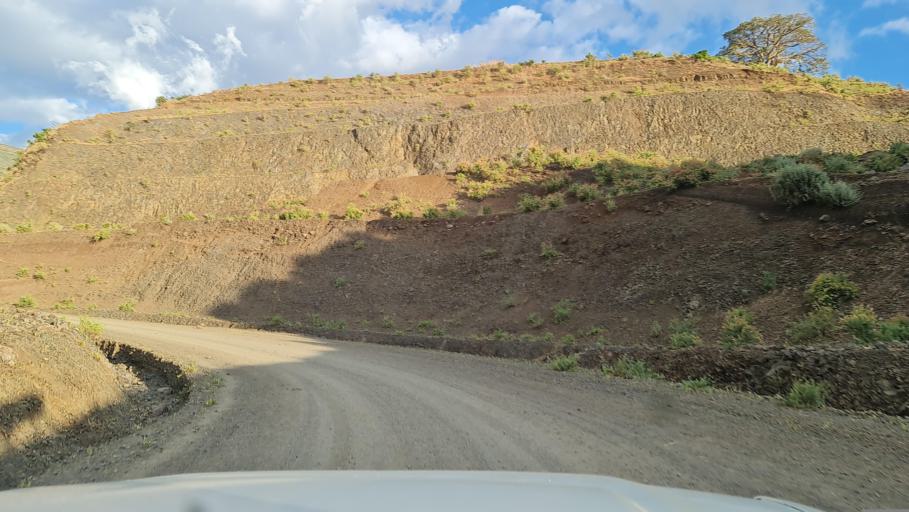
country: ET
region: Amhara
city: Debark'
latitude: 13.0266
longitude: 38.0527
